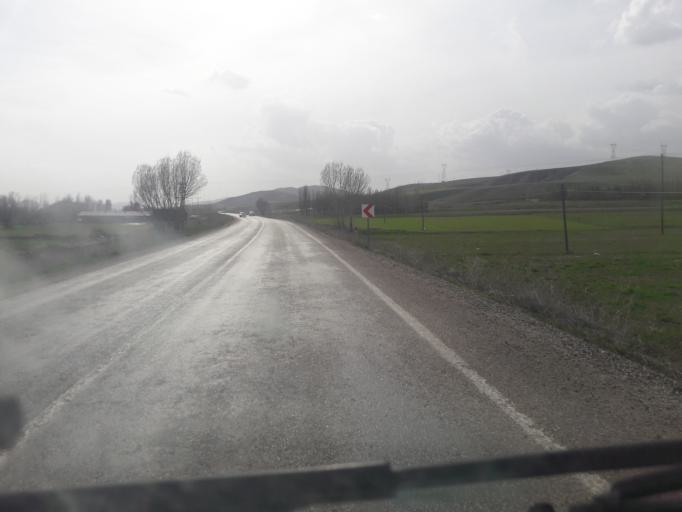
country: TR
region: Gumushane
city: Kelkit
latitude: 40.1435
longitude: 39.4138
